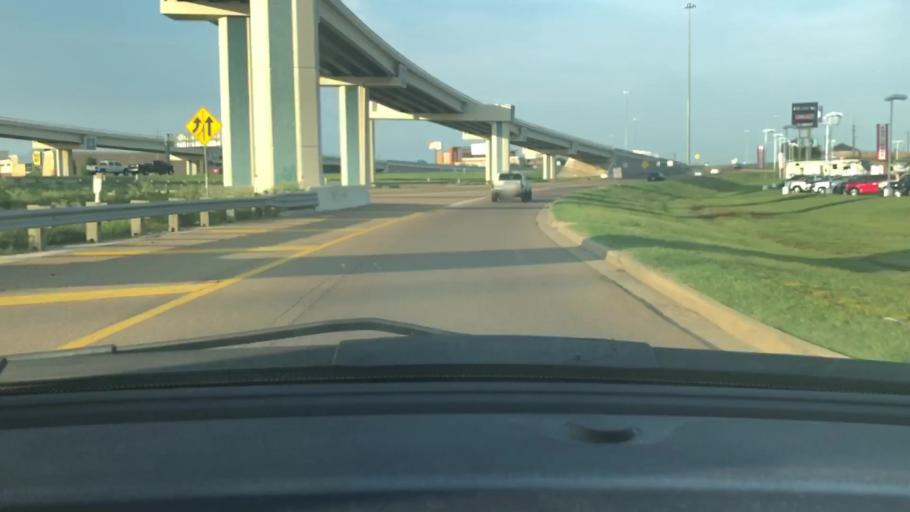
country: US
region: Texas
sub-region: Bowie County
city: Wake Village
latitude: 33.4521
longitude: -94.0960
